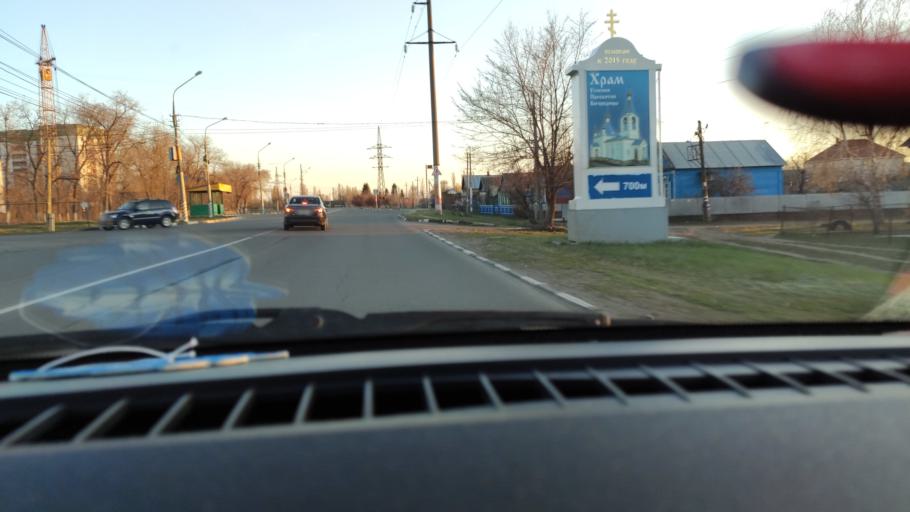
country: RU
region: Saratov
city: Privolzhskiy
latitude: 51.3949
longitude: 46.0339
